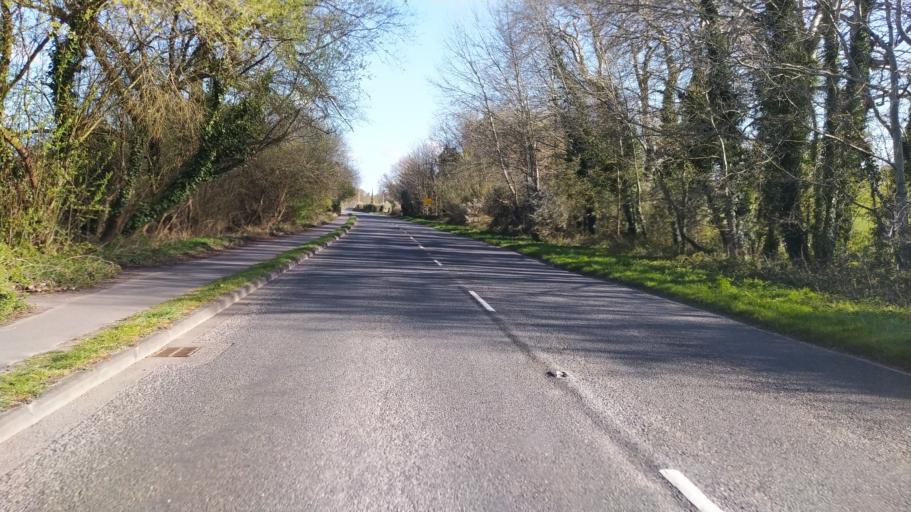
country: GB
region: England
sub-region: Hampshire
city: Abbotts Ann
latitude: 51.1191
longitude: -1.4854
